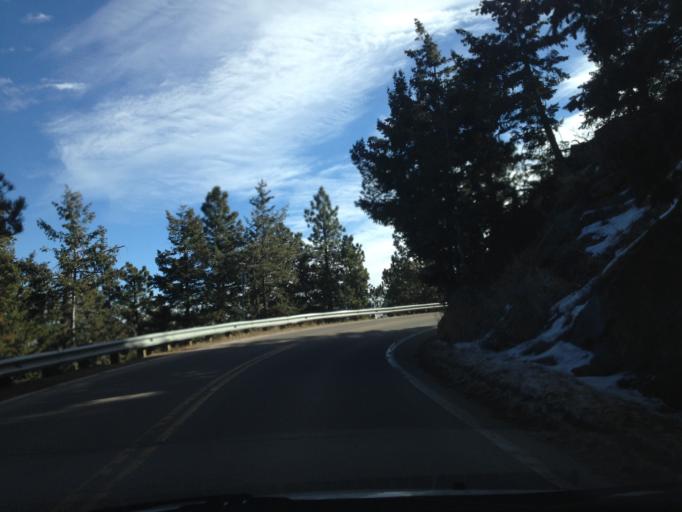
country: US
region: Colorado
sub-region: Boulder County
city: Boulder
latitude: 40.0035
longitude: -105.2946
